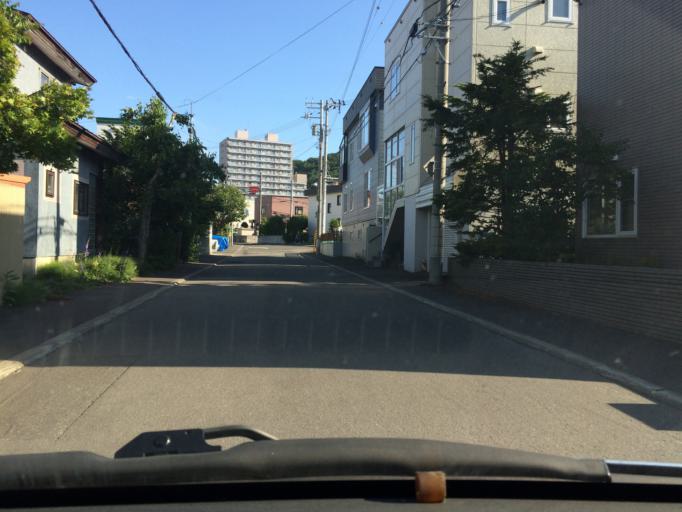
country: JP
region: Hokkaido
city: Sapporo
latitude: 43.0265
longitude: 141.3419
